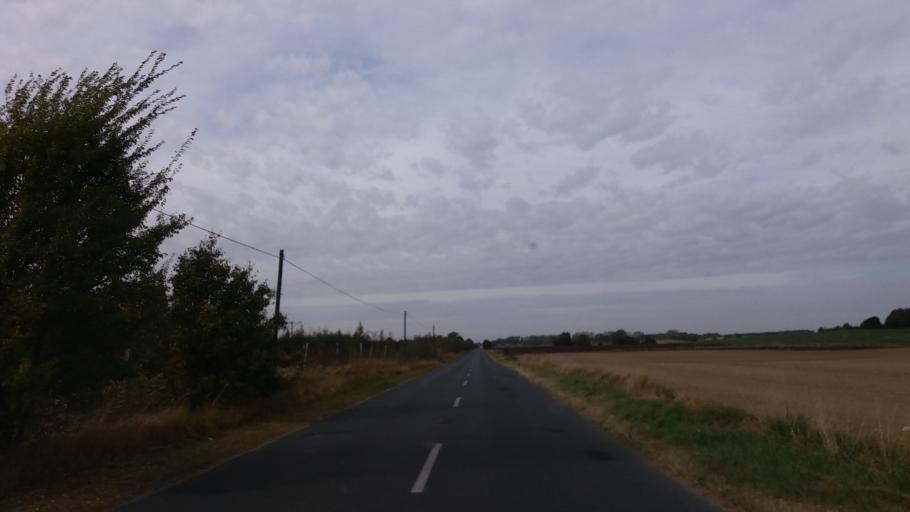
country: PL
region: Lubusz
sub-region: Powiat strzelecko-drezdenecki
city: Strzelce Krajenskie
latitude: 52.9325
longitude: 15.4728
